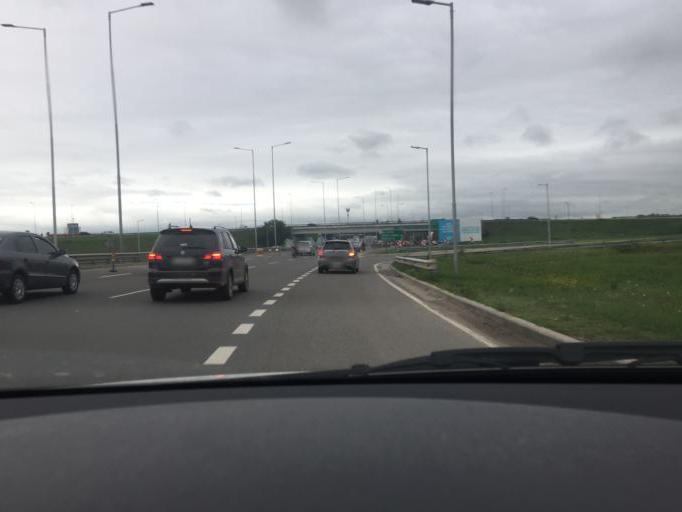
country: AR
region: Cordoba
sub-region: Departamento de Capital
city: Cordoba
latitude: -31.3521
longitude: -64.2027
